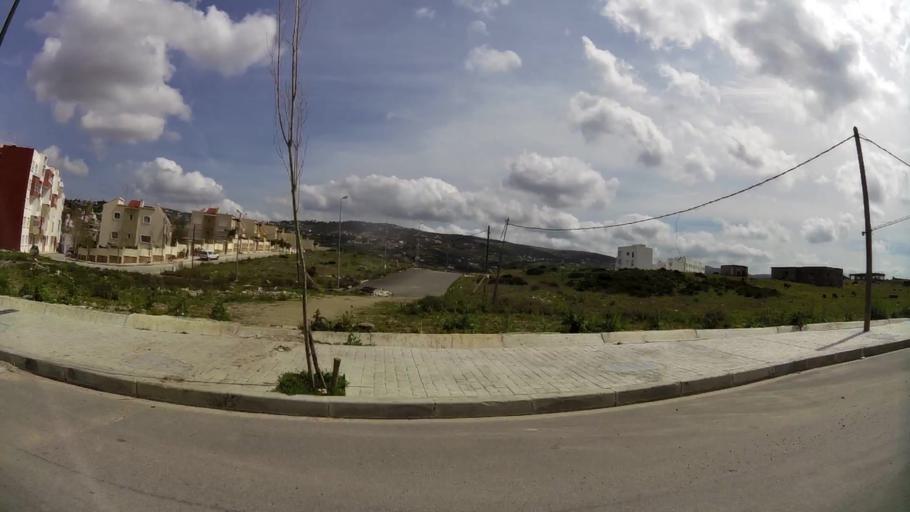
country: MA
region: Tanger-Tetouan
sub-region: Tanger-Assilah
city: Tangier
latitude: 35.7604
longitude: -5.7559
